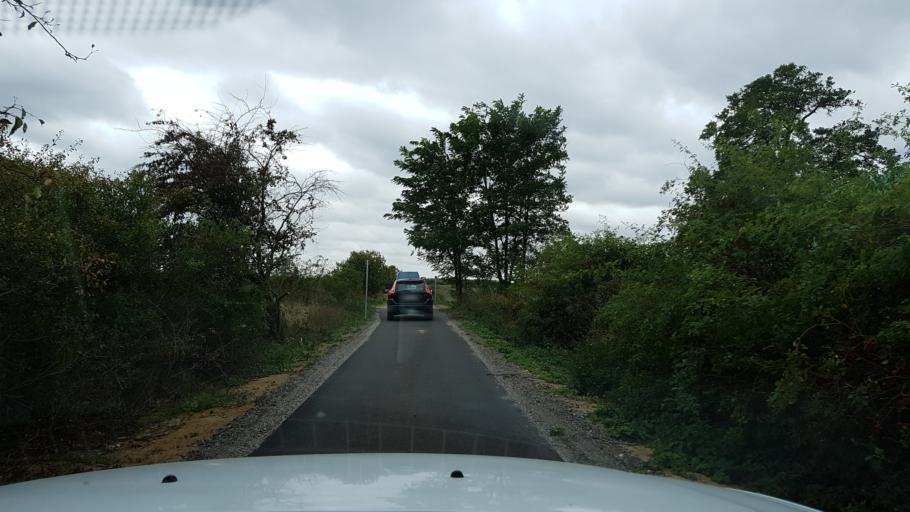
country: PL
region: West Pomeranian Voivodeship
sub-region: Powiat gryfinski
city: Cedynia
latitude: 52.8571
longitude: 14.2830
